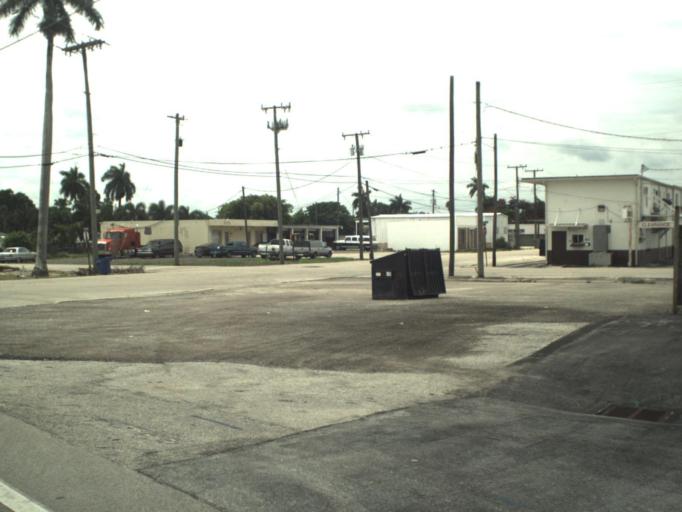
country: US
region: Florida
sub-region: Palm Beach County
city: Belle Glade
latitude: 26.6854
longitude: -80.6666
